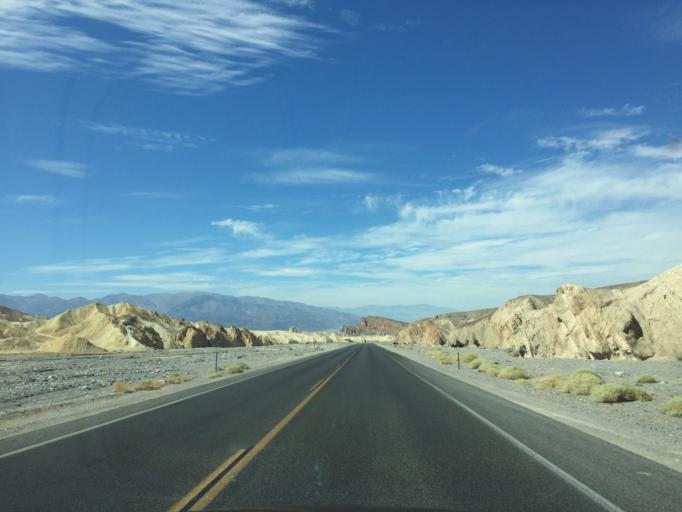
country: US
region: Nevada
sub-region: Nye County
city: Beatty
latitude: 36.4087
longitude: -116.7931
